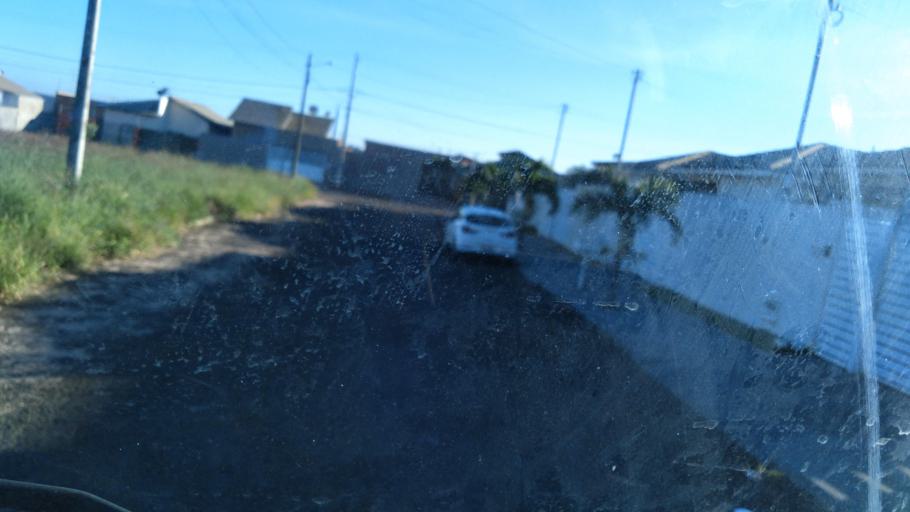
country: BR
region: Goias
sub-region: Mineiros
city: Mineiros
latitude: -17.5439
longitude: -52.5552
